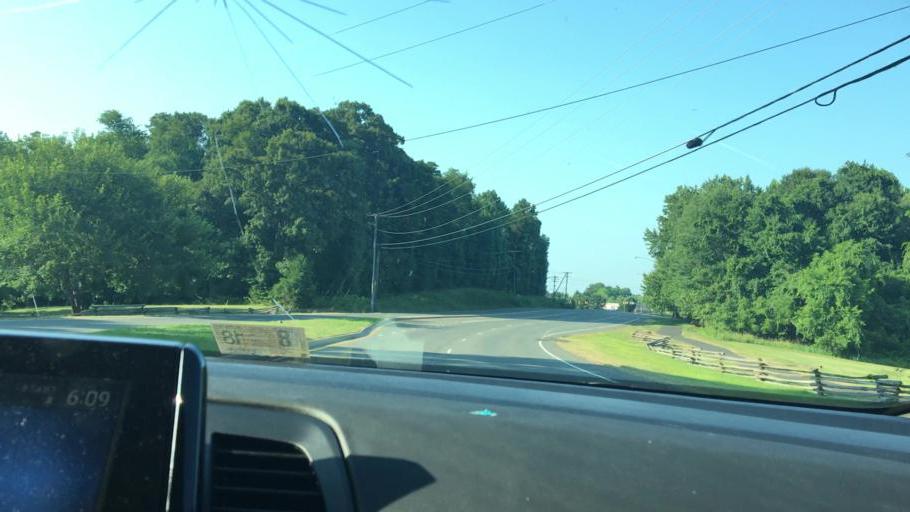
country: US
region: Virginia
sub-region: Prince William County
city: Buckhall
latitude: 38.7549
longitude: -77.4380
